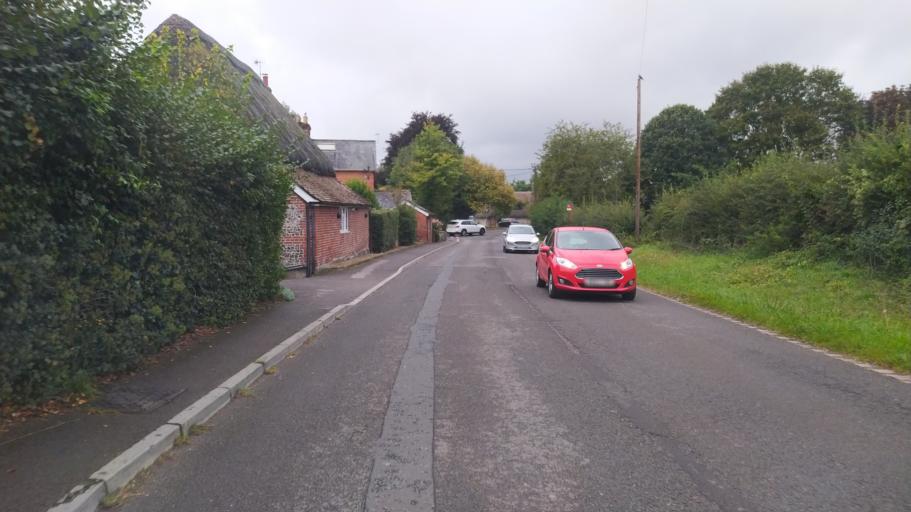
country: GB
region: England
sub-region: Wiltshire
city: Allington
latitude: 51.1166
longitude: -1.7430
